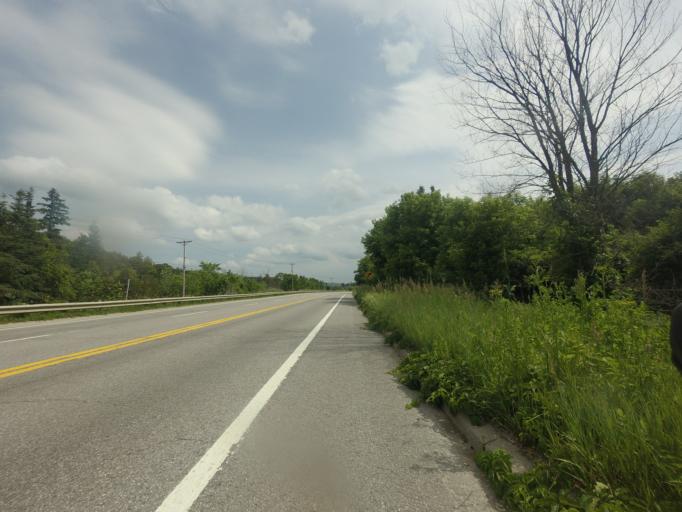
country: CA
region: Quebec
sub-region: Outaouais
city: Wakefield
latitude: 45.7525
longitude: -75.9156
